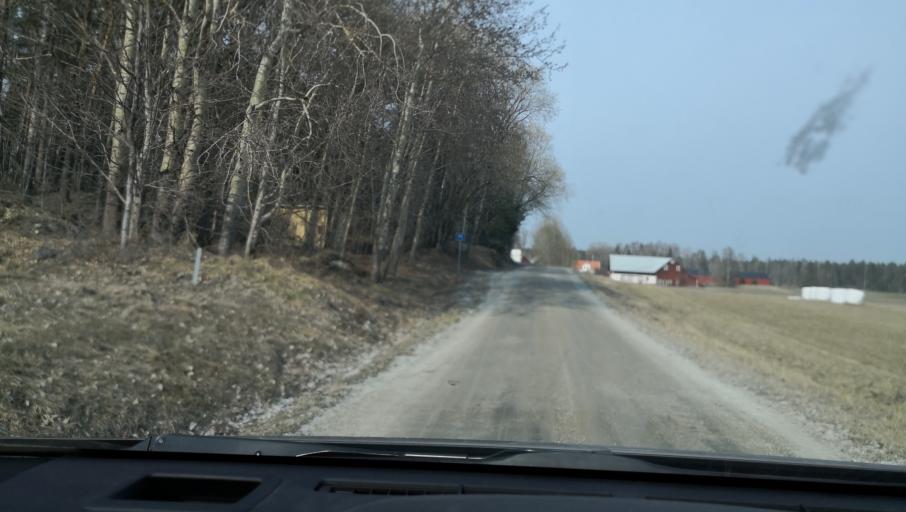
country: SE
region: OErebro
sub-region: Lindesbergs Kommun
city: Frovi
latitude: 59.3485
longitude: 15.4387
